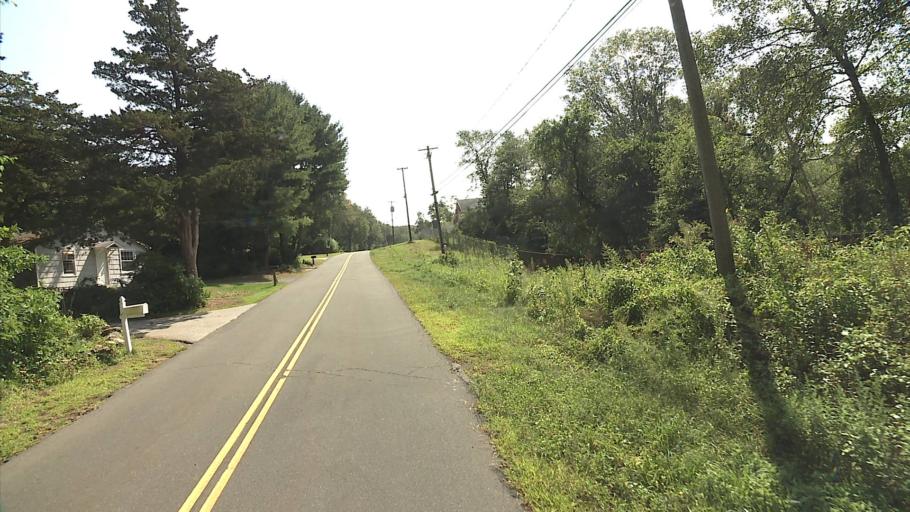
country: US
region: Connecticut
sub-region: New London County
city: Niantic
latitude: 41.3534
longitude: -72.2576
